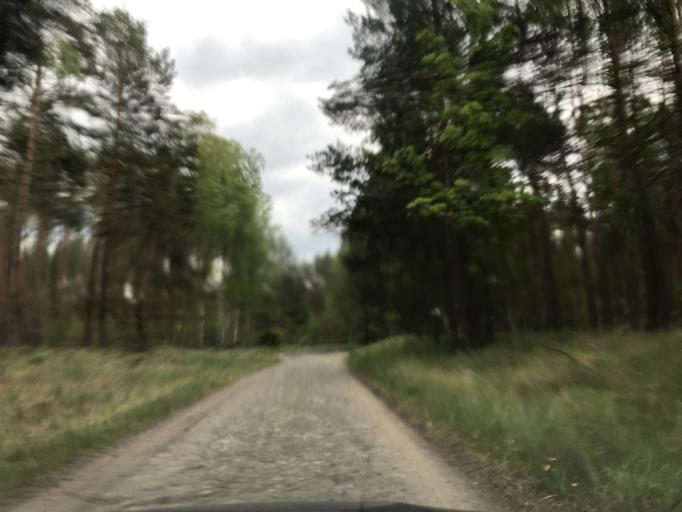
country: PL
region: West Pomeranian Voivodeship
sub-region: Powiat mysliborski
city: Mysliborz
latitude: 52.8721
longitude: 14.8743
